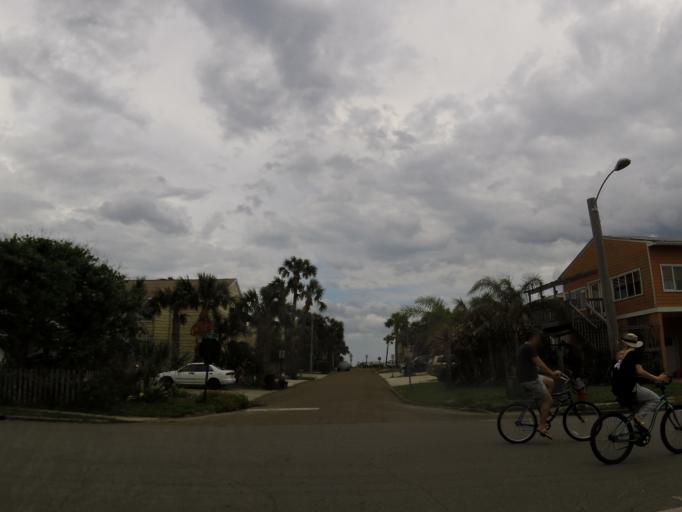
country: US
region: Florida
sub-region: Duval County
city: Neptune Beach
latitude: 30.3106
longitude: -81.3942
